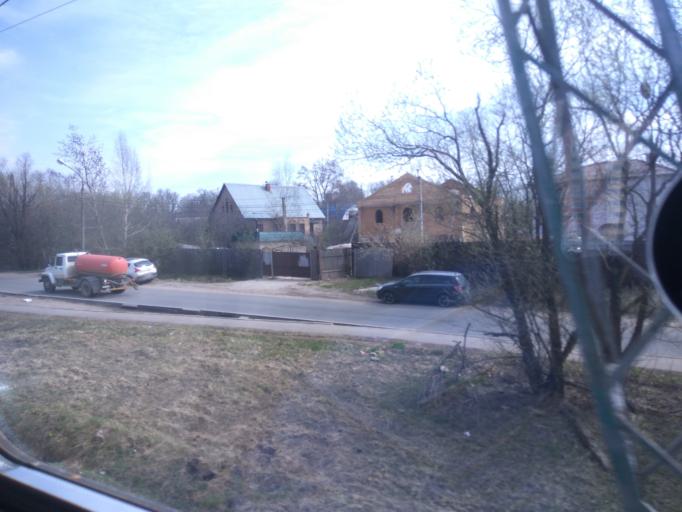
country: RU
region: Moskovskaya
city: Lobnya
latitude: 56.0196
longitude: 37.4845
